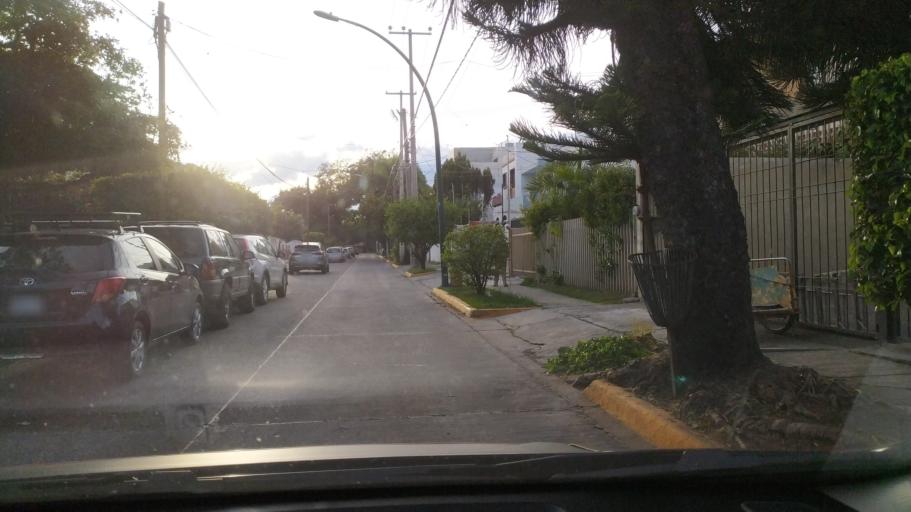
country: MX
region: Jalisco
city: Guadalajara
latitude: 20.6629
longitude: -103.4057
